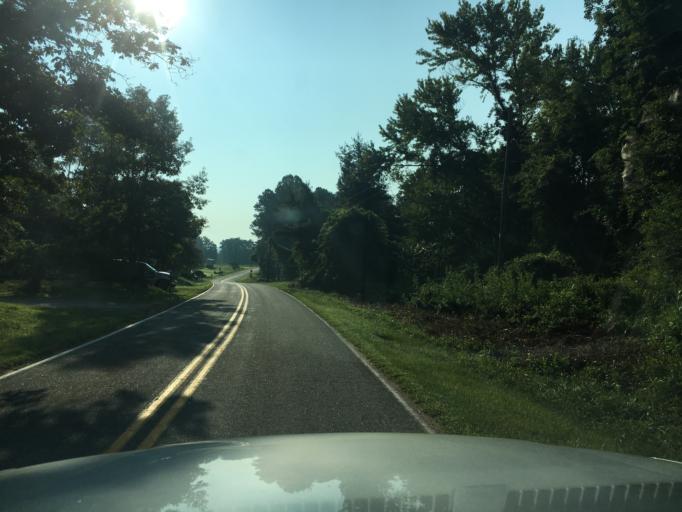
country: US
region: North Carolina
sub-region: Rutherford County
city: Rutherfordton
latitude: 35.2507
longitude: -82.0427
